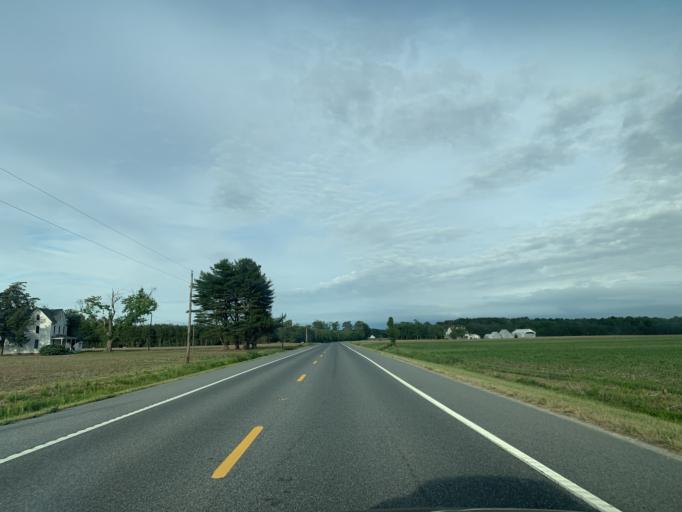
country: US
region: Virginia
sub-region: Accomack County
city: Captains Cove
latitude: 38.0696
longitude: -75.4467
